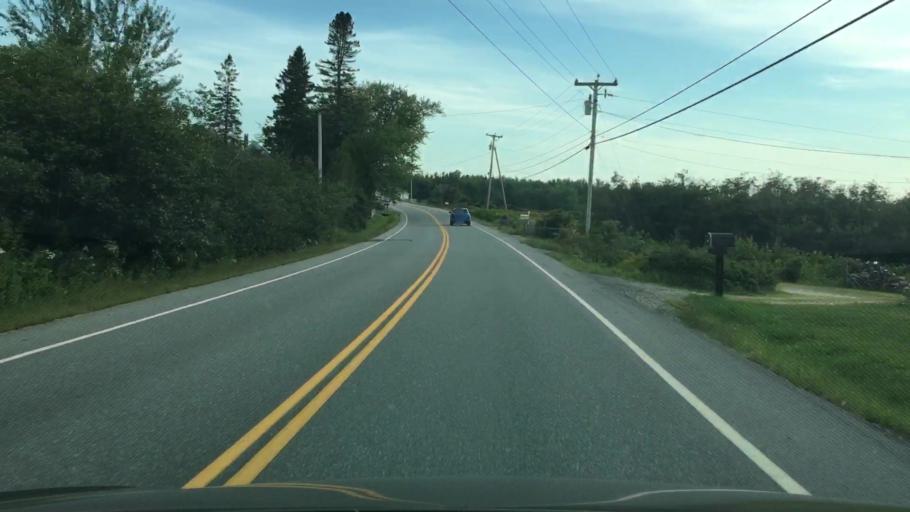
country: US
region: Maine
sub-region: Hancock County
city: Penobscot
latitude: 44.4726
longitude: -68.7808
